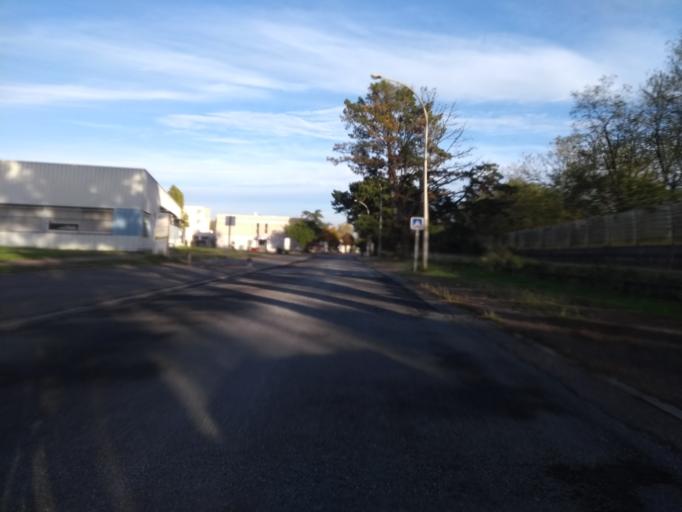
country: FR
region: Aquitaine
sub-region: Departement de la Gironde
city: Gradignan
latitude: 44.7905
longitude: -0.6110
